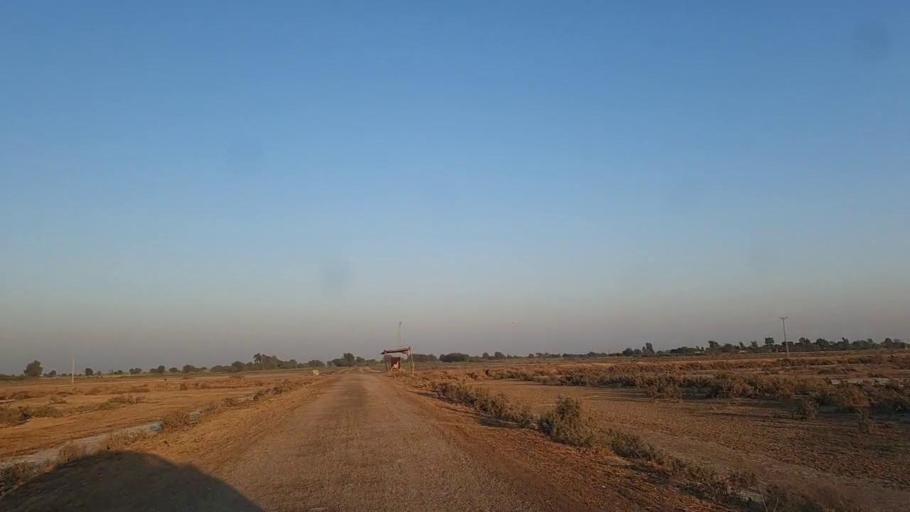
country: PK
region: Sindh
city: Samaro
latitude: 25.2976
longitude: 69.3911
